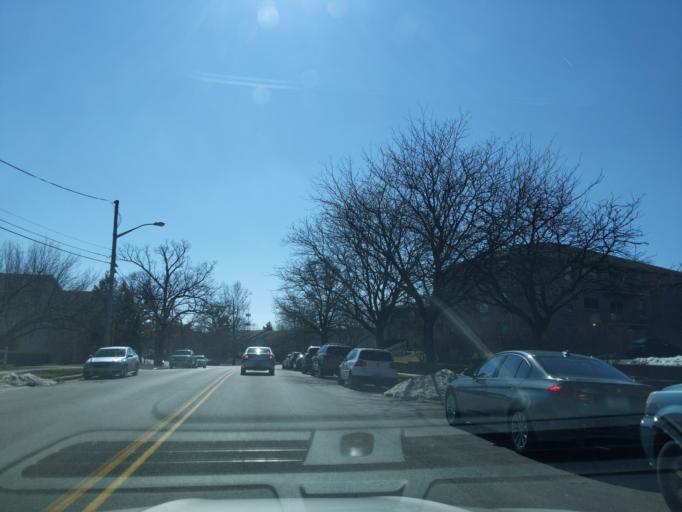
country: US
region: Indiana
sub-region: Tippecanoe County
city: West Lafayette
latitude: 40.4194
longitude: -86.9087
